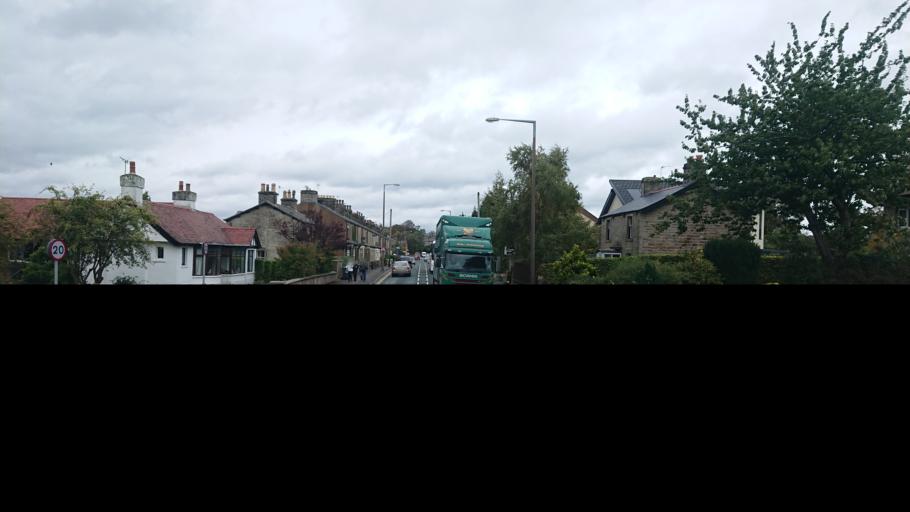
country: GB
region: England
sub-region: Lancashire
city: Lancaster
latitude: 54.0256
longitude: -2.7951
